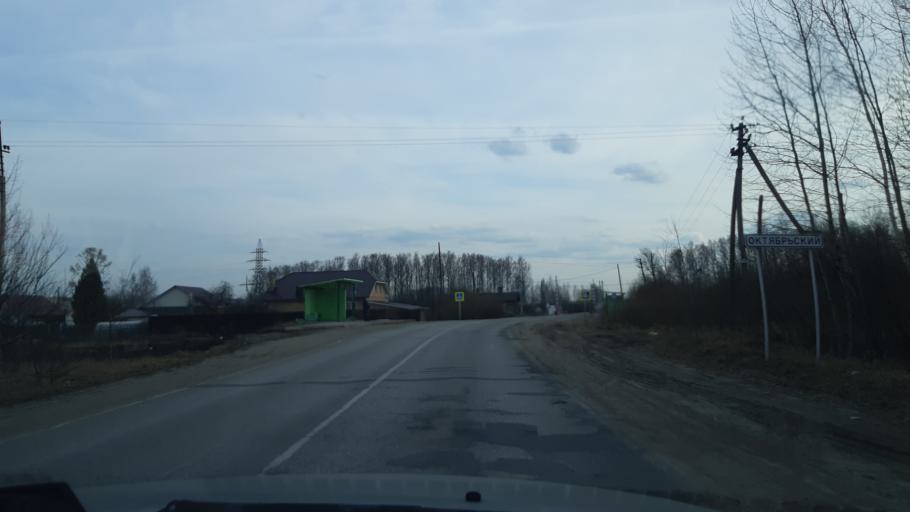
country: RU
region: Vladimir
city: Luknovo
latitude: 56.2244
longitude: 42.0349
